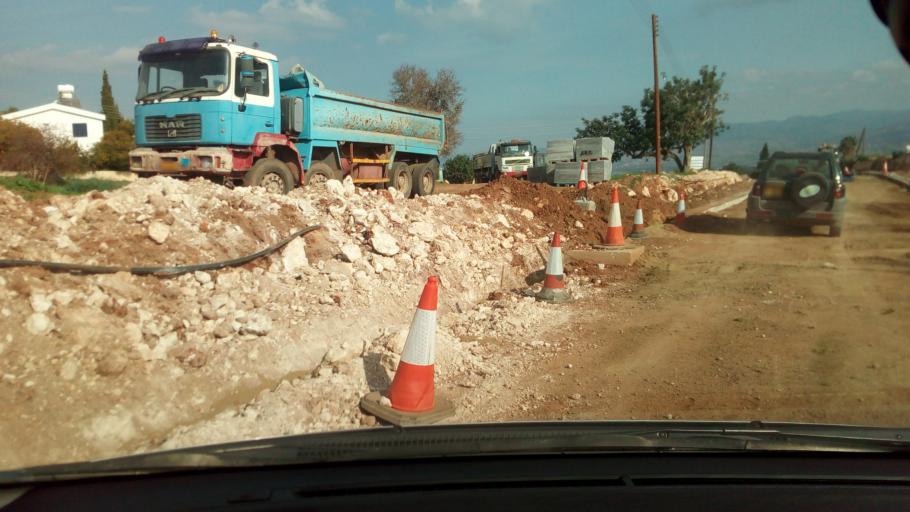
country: CY
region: Pafos
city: Polis
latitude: 35.0250
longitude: 32.3582
